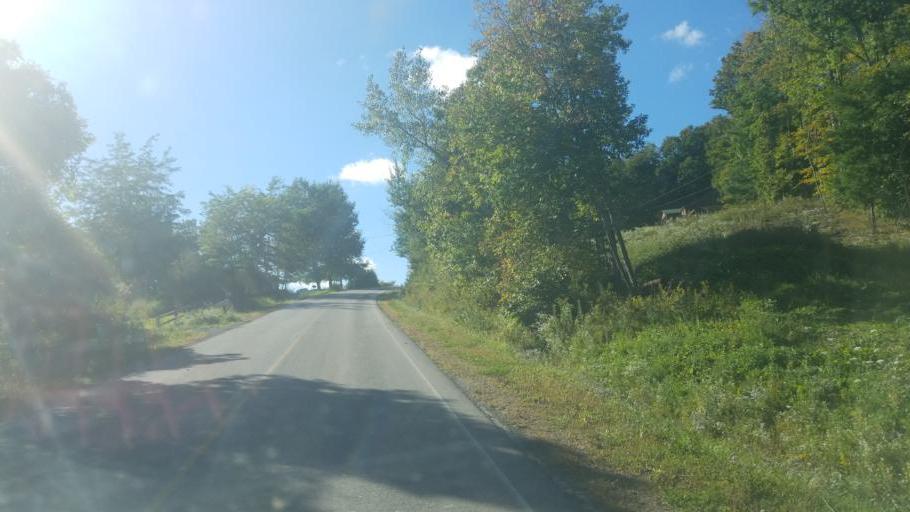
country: US
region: New York
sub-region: Allegany County
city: Friendship
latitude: 42.2759
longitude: -78.1525
